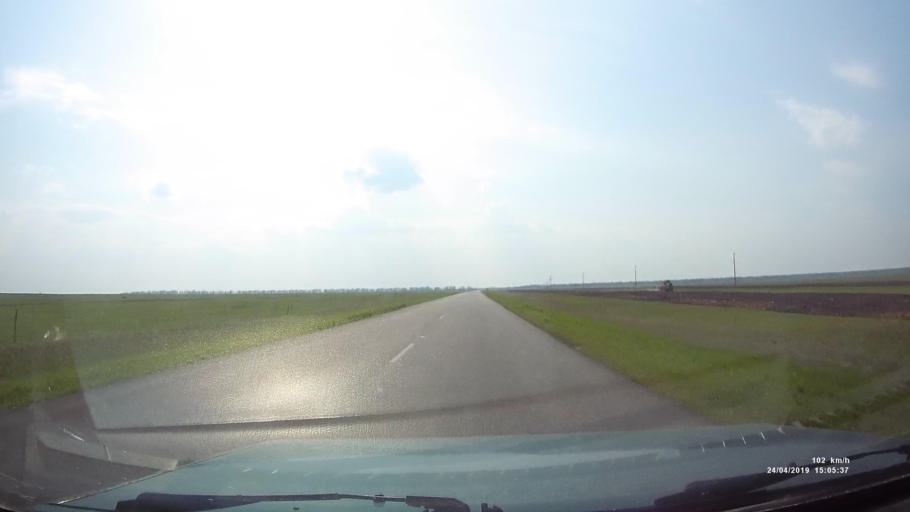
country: RU
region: Rostov
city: Remontnoye
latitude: 46.5598
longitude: 43.4451
